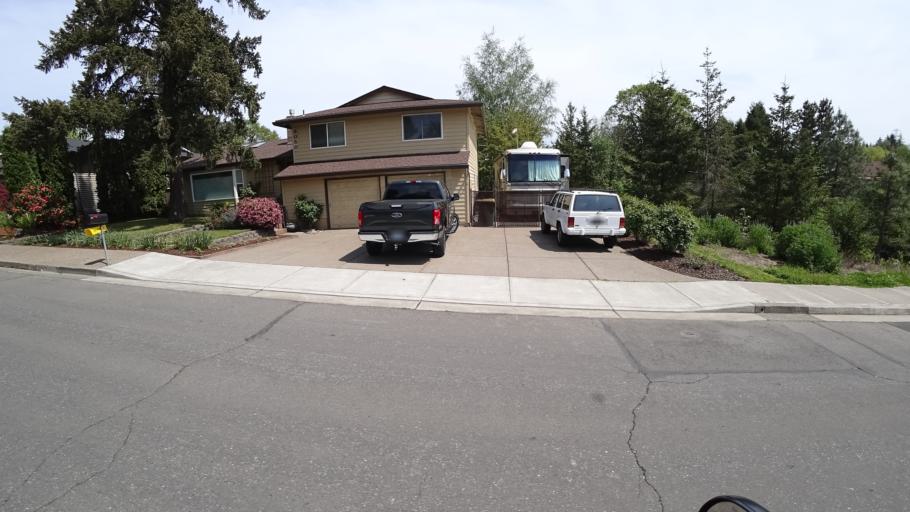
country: US
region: Oregon
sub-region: Washington County
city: Aloha
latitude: 45.4617
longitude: -122.8451
